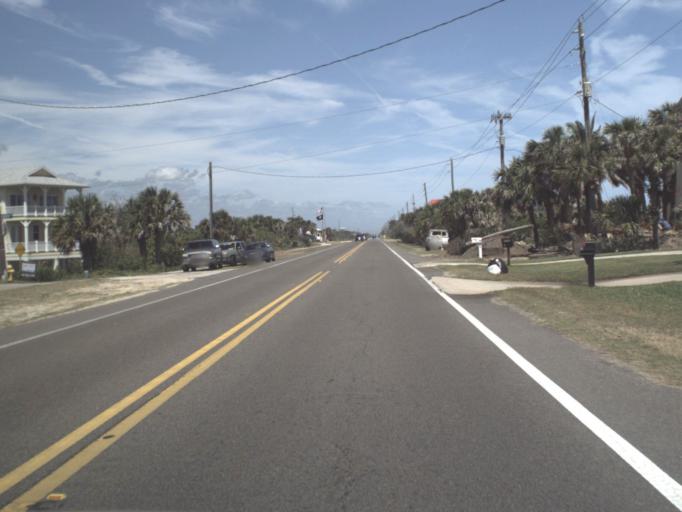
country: US
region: Florida
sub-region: Flagler County
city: Flagler Beach
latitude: 29.5251
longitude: -81.1496
